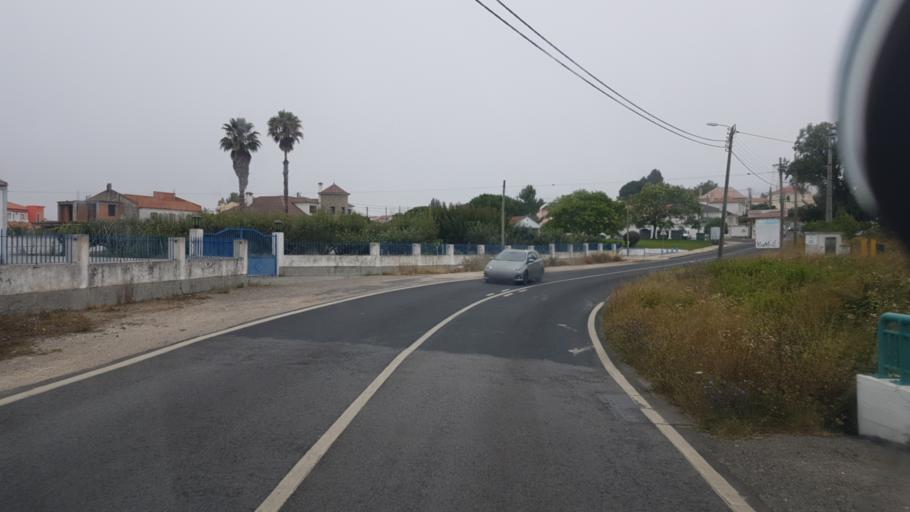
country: PT
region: Lisbon
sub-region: Sintra
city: Sintra
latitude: 38.8304
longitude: -9.3706
